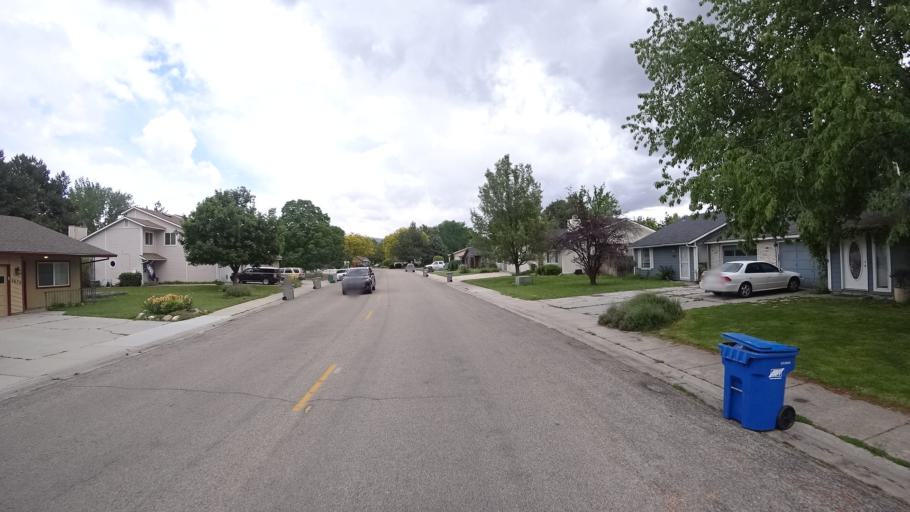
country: US
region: Idaho
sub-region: Ada County
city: Garden City
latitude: 43.6597
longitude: -116.2595
